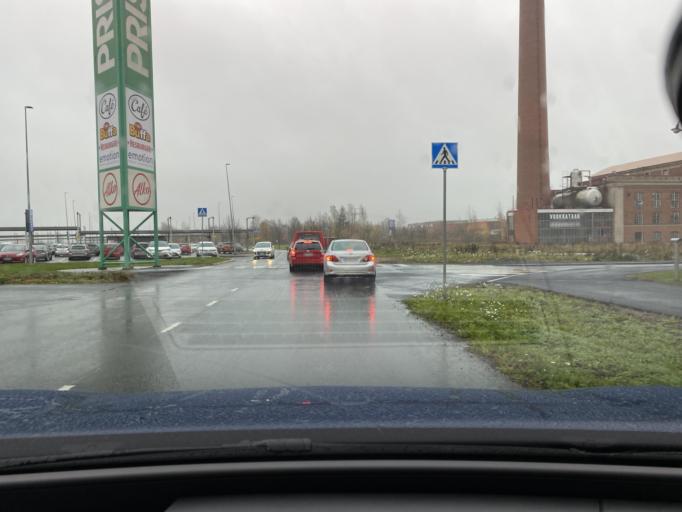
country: FI
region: Haeme
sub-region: Forssa
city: Forssa
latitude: 60.8114
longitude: 23.6332
